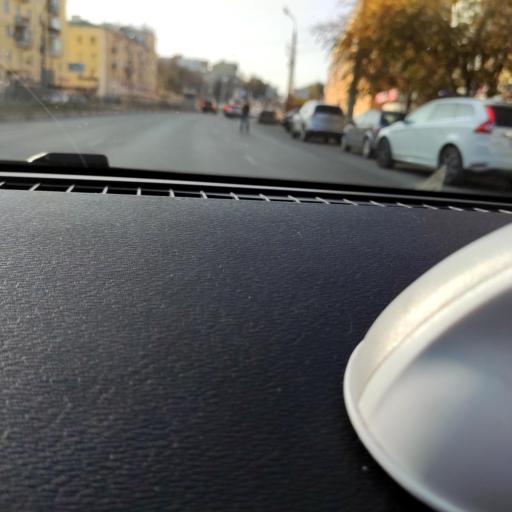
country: RU
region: Samara
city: Samara
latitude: 53.2013
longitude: 50.2242
